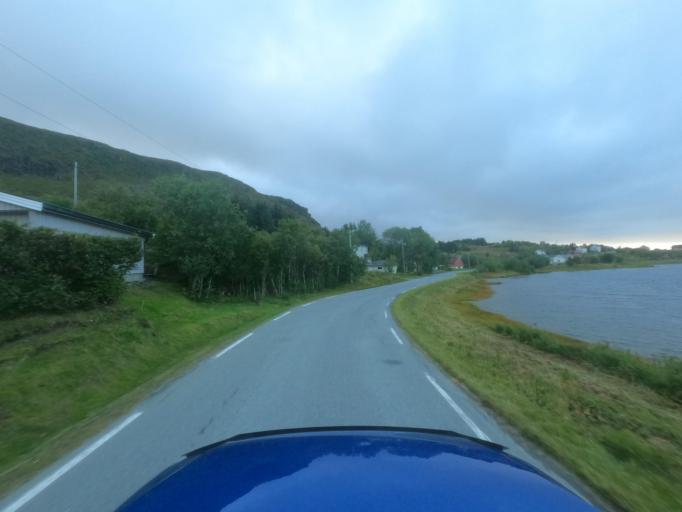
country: NO
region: Nordland
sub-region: Vestvagoy
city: Evjen
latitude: 68.2569
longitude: 13.7795
